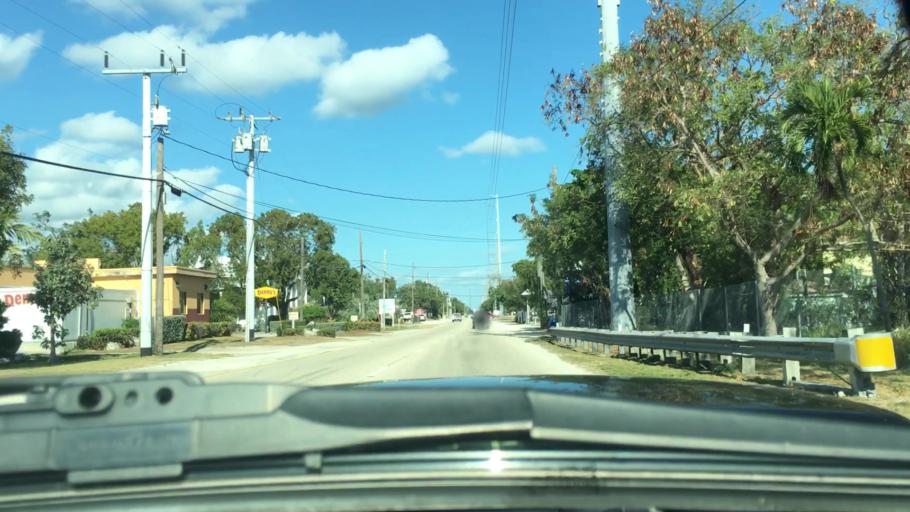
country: US
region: Florida
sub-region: Monroe County
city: Key Largo
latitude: 25.0747
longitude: -80.4619
